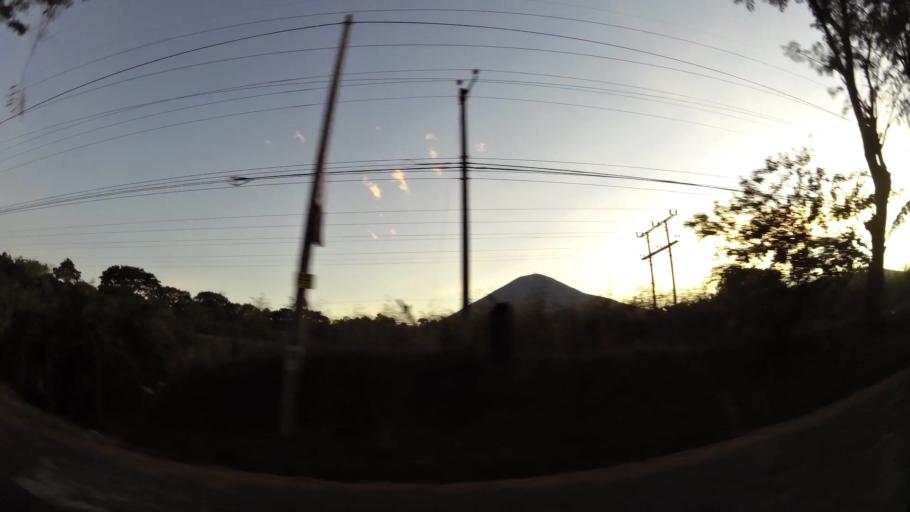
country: SV
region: San Miguel
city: Moncagua
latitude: 13.5040
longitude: -88.2252
